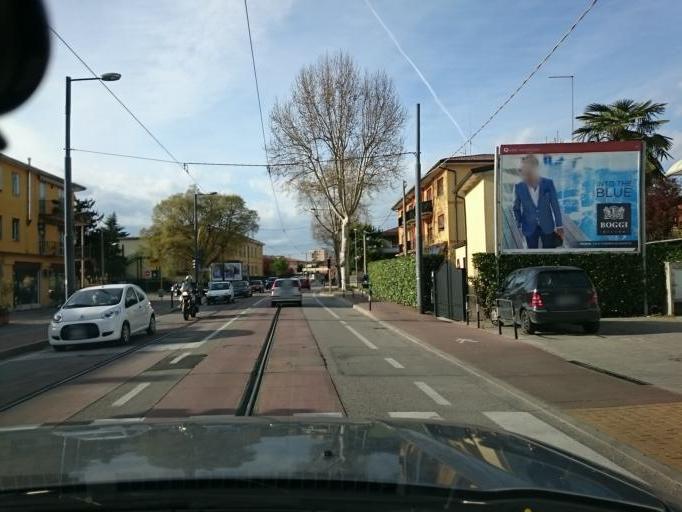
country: IT
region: Veneto
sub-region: Provincia di Padova
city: Mandriola-Sant'Agostino
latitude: 45.3729
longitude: 11.8712
